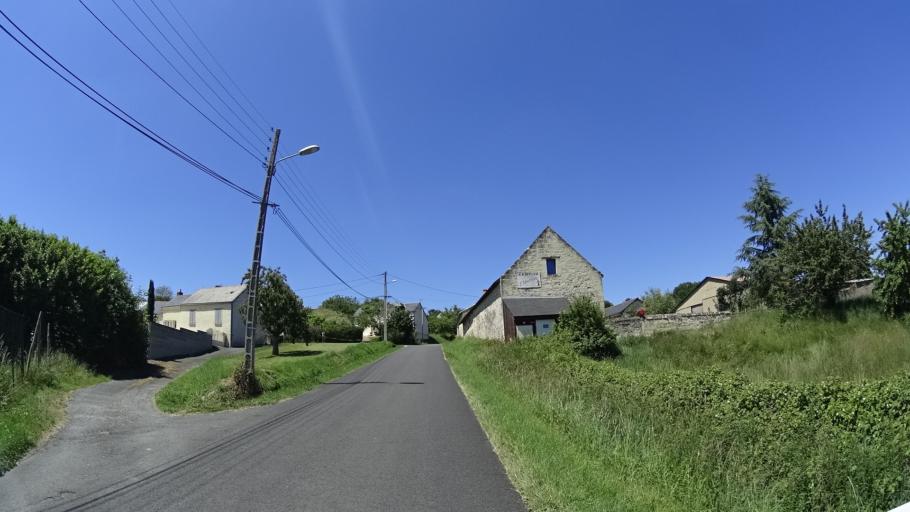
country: FR
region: Pays de la Loire
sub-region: Departement de Maine-et-Loire
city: Saint-Martin-de-la-Place
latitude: 47.2819
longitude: -0.1330
